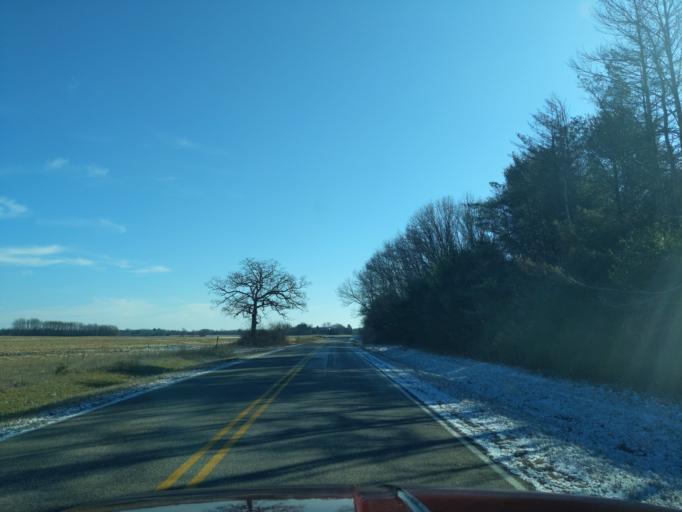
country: US
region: Wisconsin
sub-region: Waushara County
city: Silver Lake
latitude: 44.0917
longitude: -89.1792
